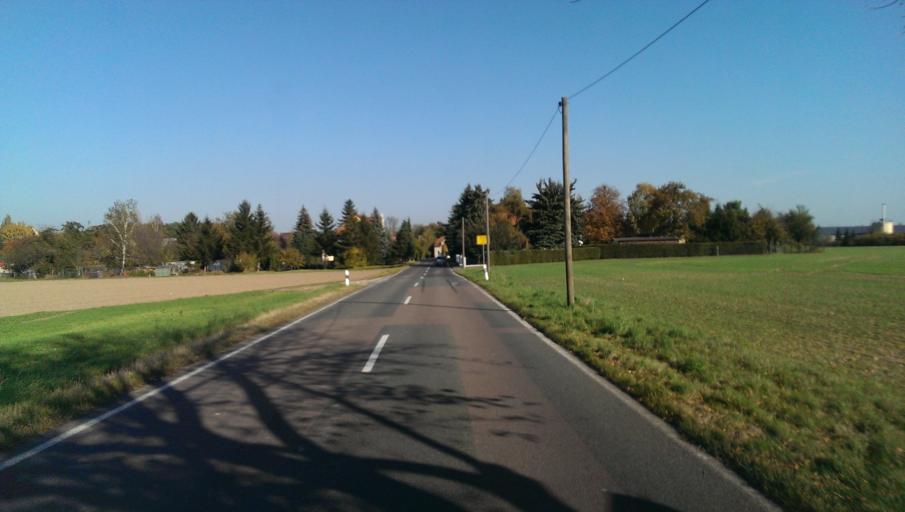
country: DE
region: Saxony
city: Stauchitz
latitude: 51.2802
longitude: 13.2234
